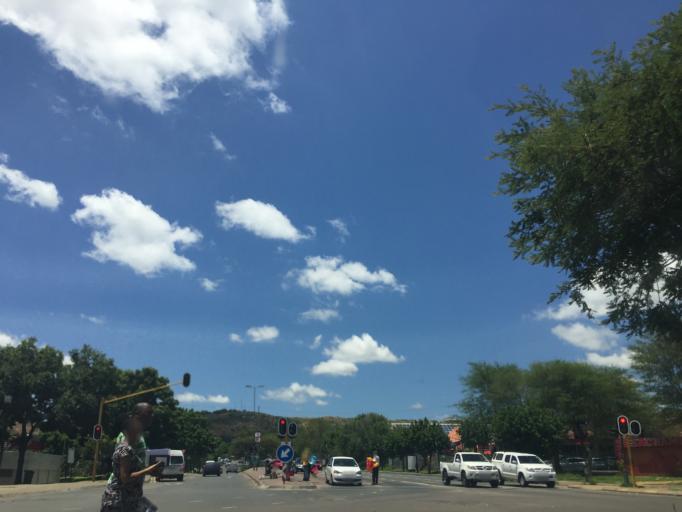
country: ZA
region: Gauteng
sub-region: City of Tshwane Metropolitan Municipality
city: Pretoria
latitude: -25.6709
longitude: 28.1084
